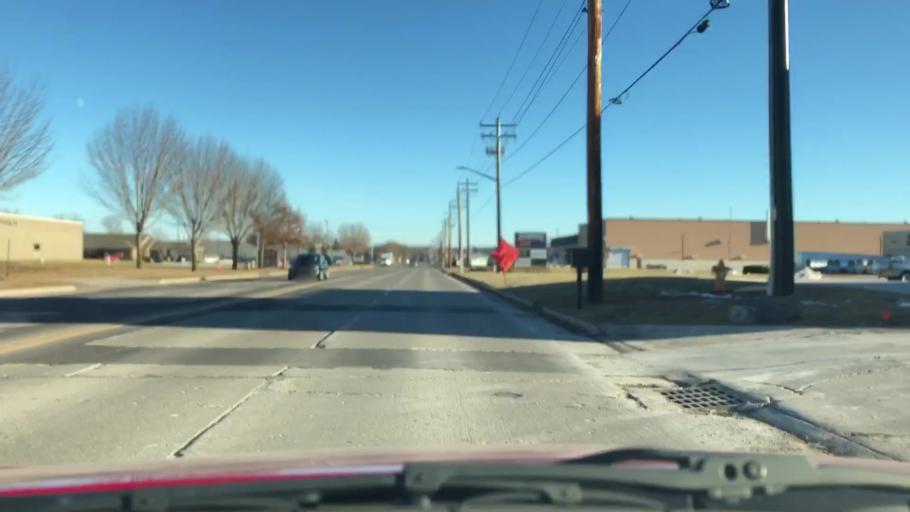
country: US
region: Wisconsin
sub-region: Brown County
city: Ashwaubenon
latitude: 44.4873
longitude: -88.0590
